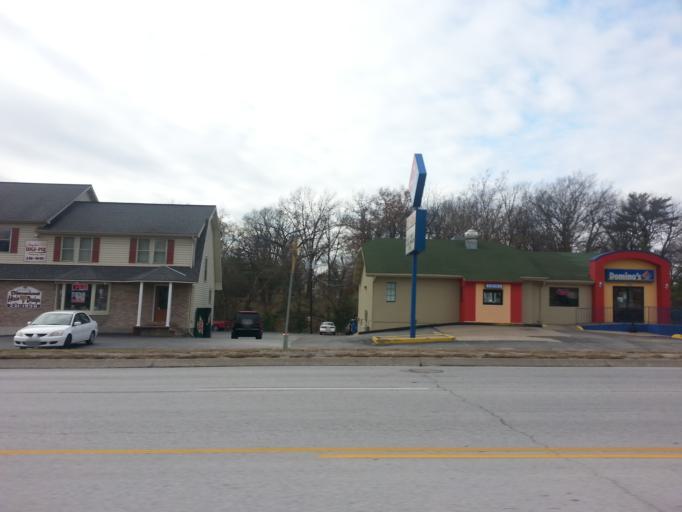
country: US
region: Missouri
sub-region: Marion County
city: Hannibal
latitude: 39.7195
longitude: -91.3920
